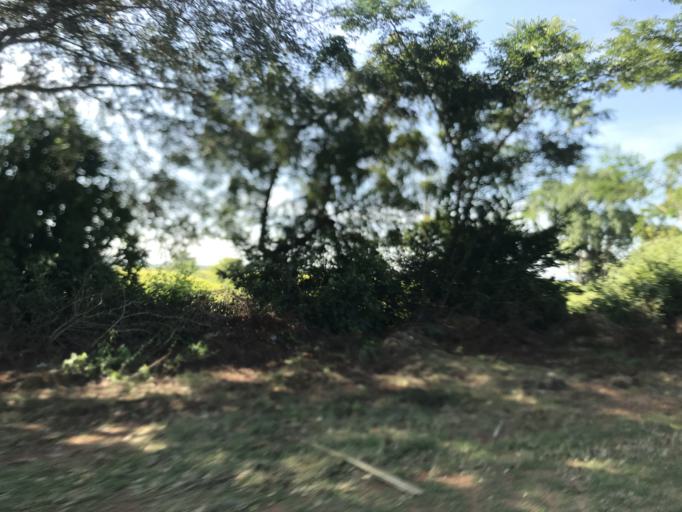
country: IN
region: Karnataka
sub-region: Mysore
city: Heggadadevankote
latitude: 12.1259
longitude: 76.4590
